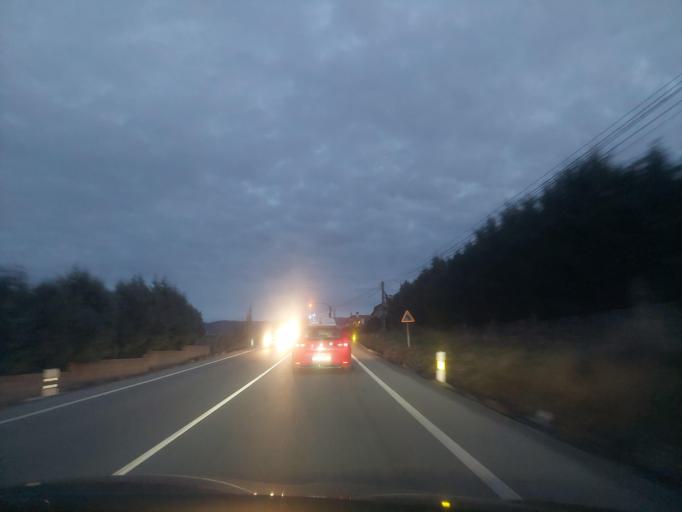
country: ES
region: Castille and Leon
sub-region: Provincia de Segovia
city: La Lastrilla
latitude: 40.9526
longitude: -4.1019
